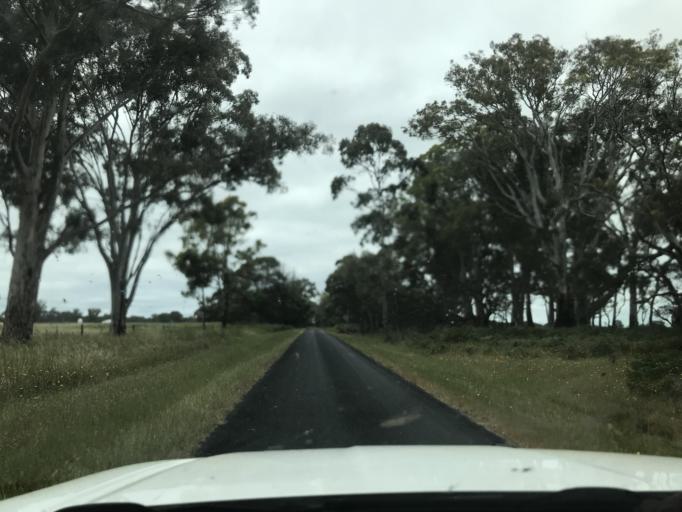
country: AU
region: South Australia
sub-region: Wattle Range
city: Penola
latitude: -37.2007
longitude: 140.9714
